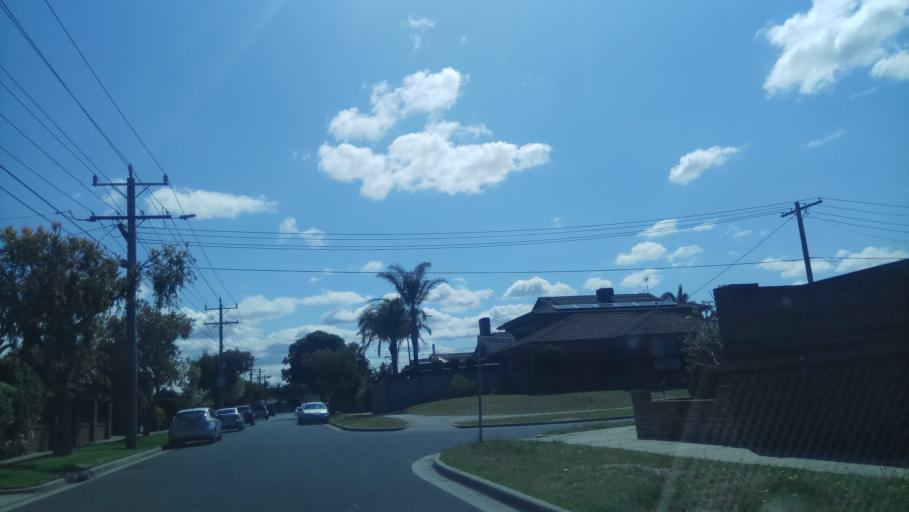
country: AU
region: Victoria
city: Heatherton
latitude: -37.9653
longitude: 145.0825
